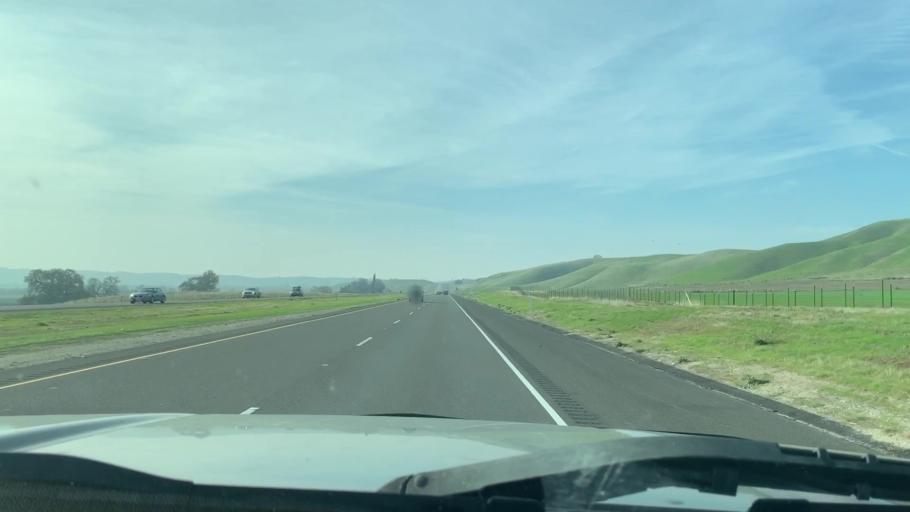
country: US
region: California
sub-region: San Luis Obispo County
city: Shandon
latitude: 35.6611
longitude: -120.4544
